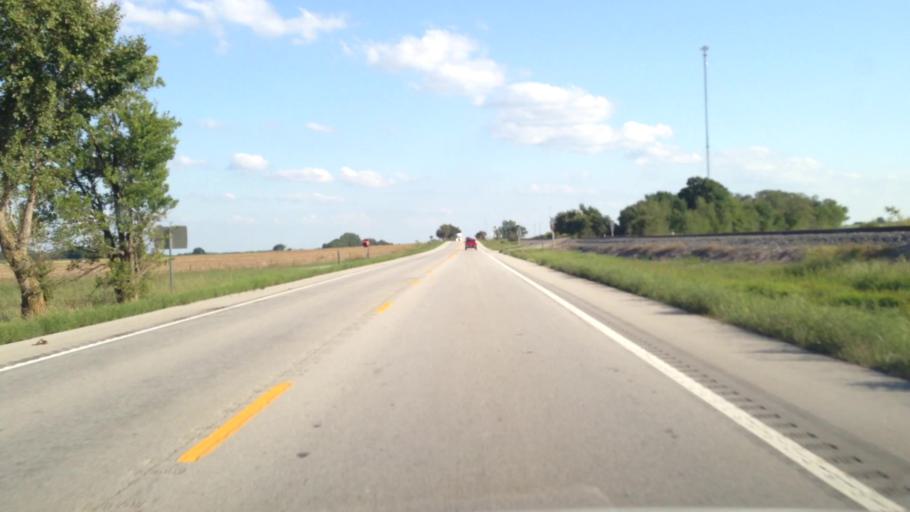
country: US
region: Missouri
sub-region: Jasper County
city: Carl Junction
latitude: 37.2653
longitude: -94.5961
